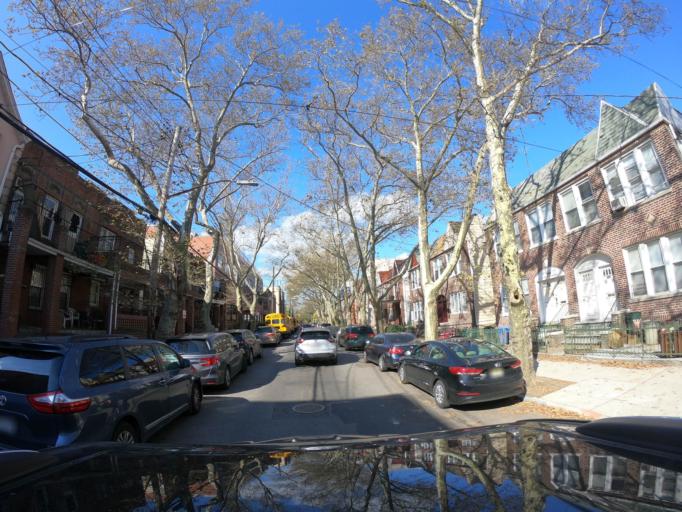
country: US
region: New York
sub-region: Kings County
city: Bensonhurst
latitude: 40.6253
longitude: -73.9820
